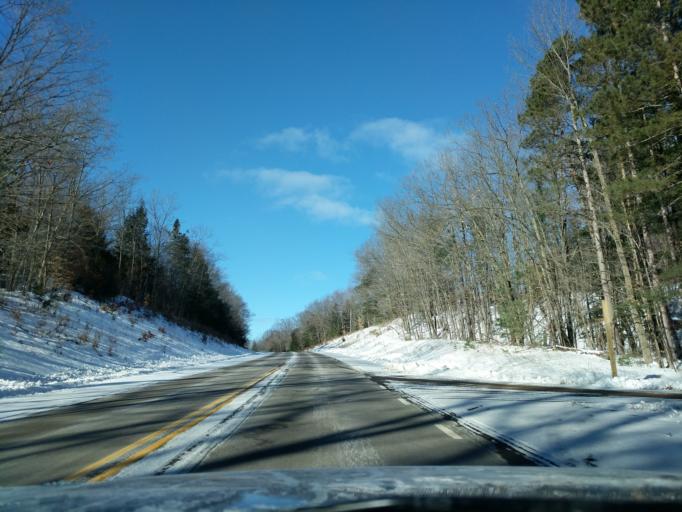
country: US
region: Wisconsin
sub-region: Menominee County
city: Keshena
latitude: 45.1458
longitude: -88.6824
